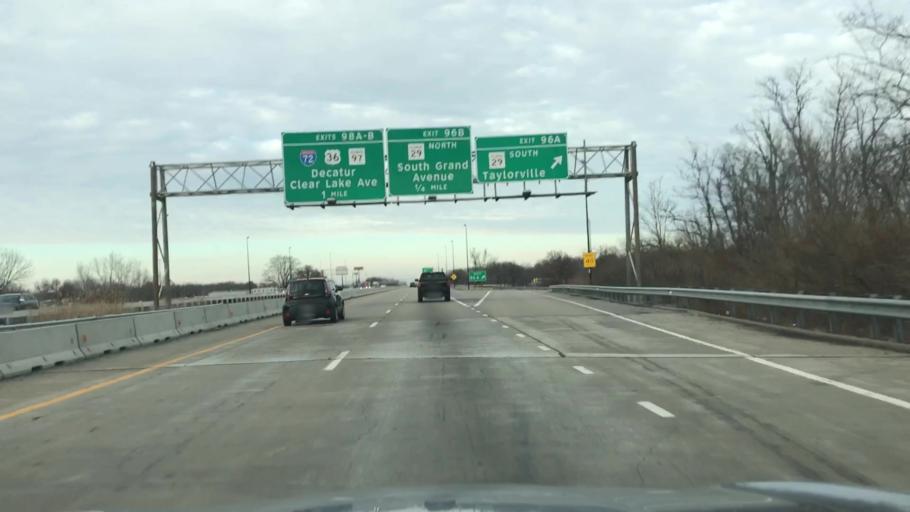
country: US
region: Illinois
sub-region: Sangamon County
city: Grandview
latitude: 39.7828
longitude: -89.6001
